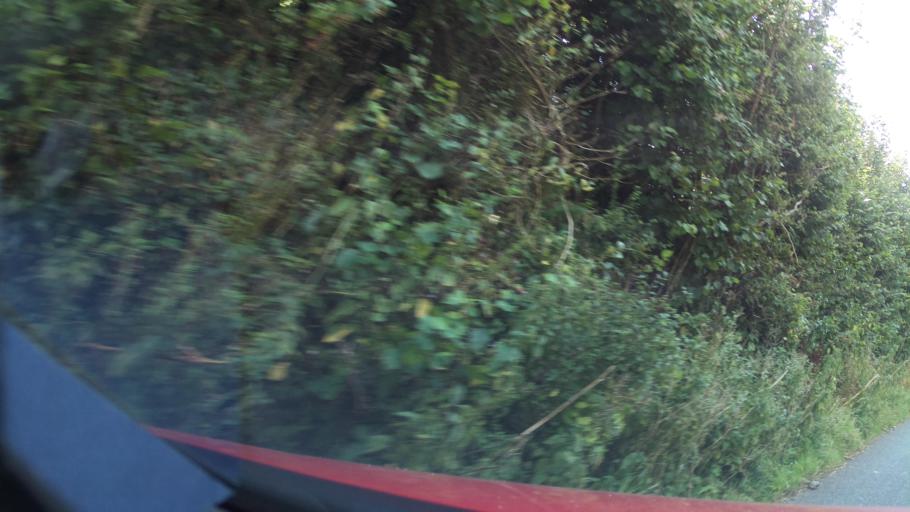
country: GB
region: England
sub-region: Devon
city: Dartmouth
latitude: 50.3641
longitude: -3.5529
